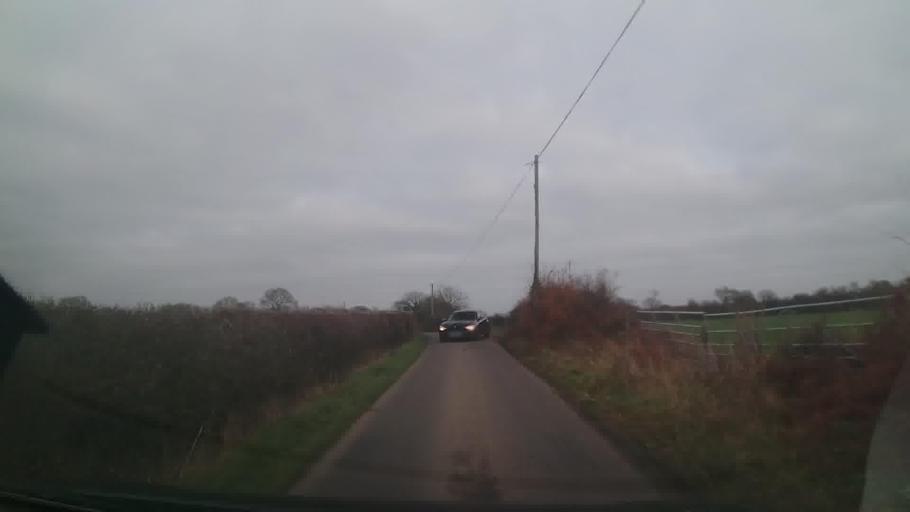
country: GB
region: England
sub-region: Shropshire
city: Petton
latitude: 52.8237
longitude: -2.7914
